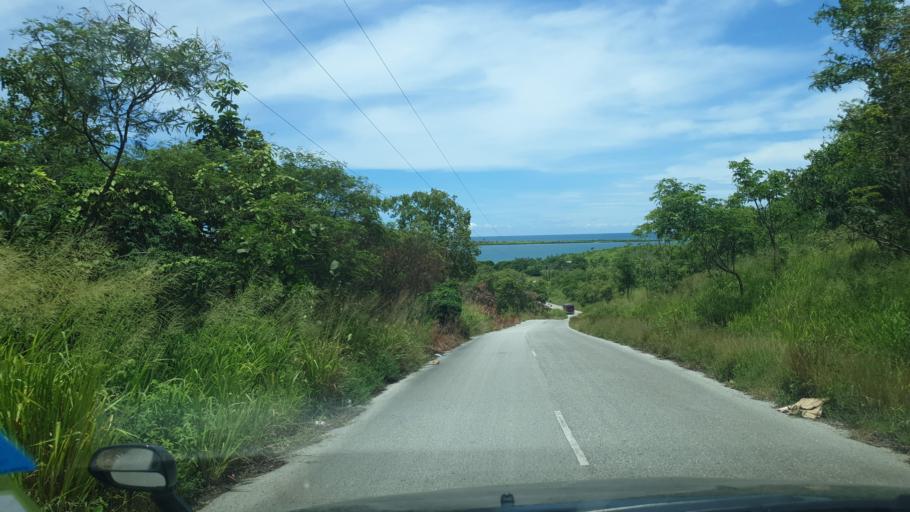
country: PG
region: National Capital
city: Port Moresby
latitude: -9.4293
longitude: 147.0595
